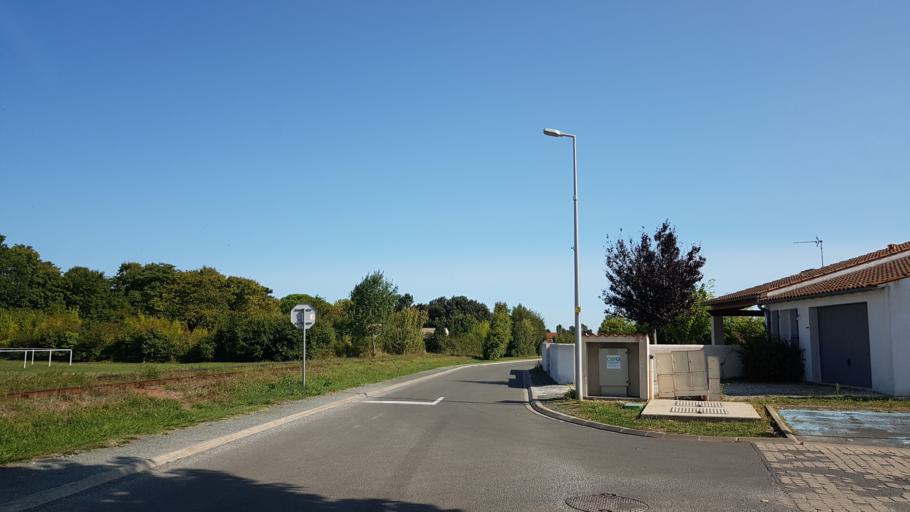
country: FR
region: Poitou-Charentes
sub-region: Departement de la Charente-Maritime
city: Breuillet
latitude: 45.7090
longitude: -1.0333
